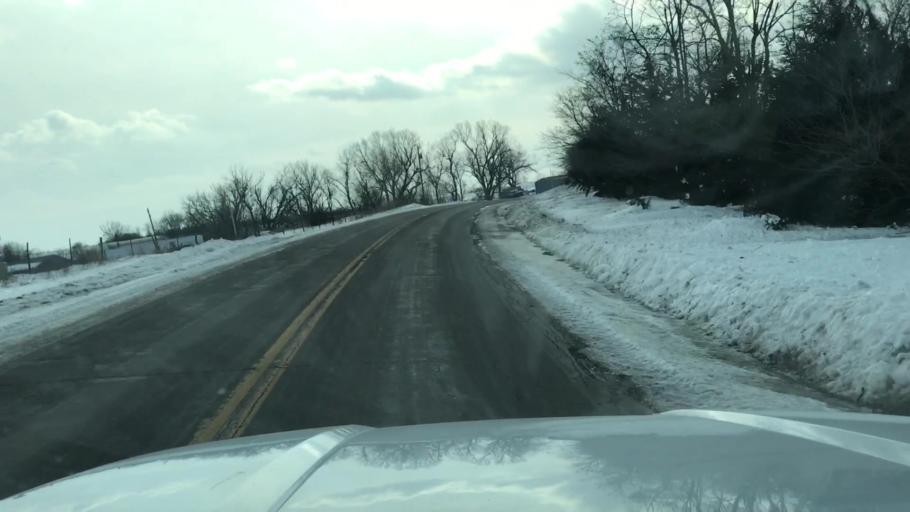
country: US
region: Missouri
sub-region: Gentry County
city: Stanberry
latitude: 40.3678
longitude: -94.6481
